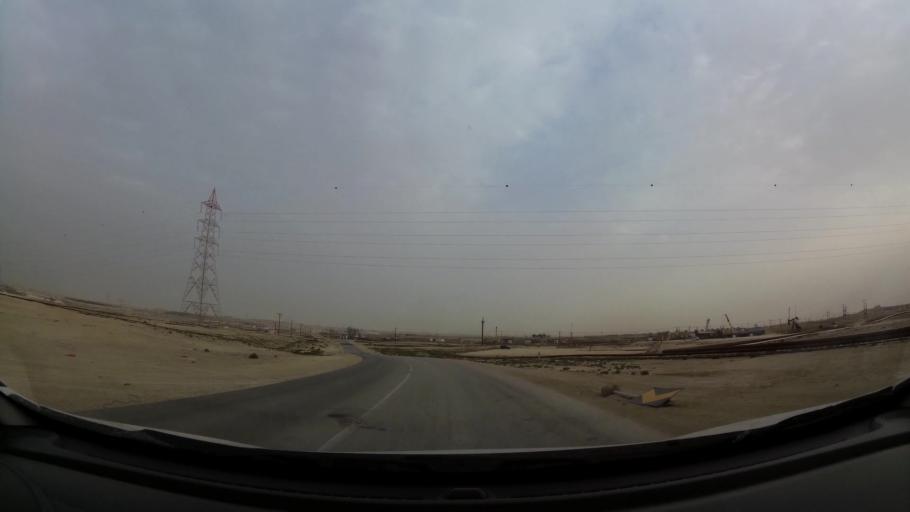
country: BH
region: Central Governorate
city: Dar Kulayb
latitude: 26.0204
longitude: 50.5721
